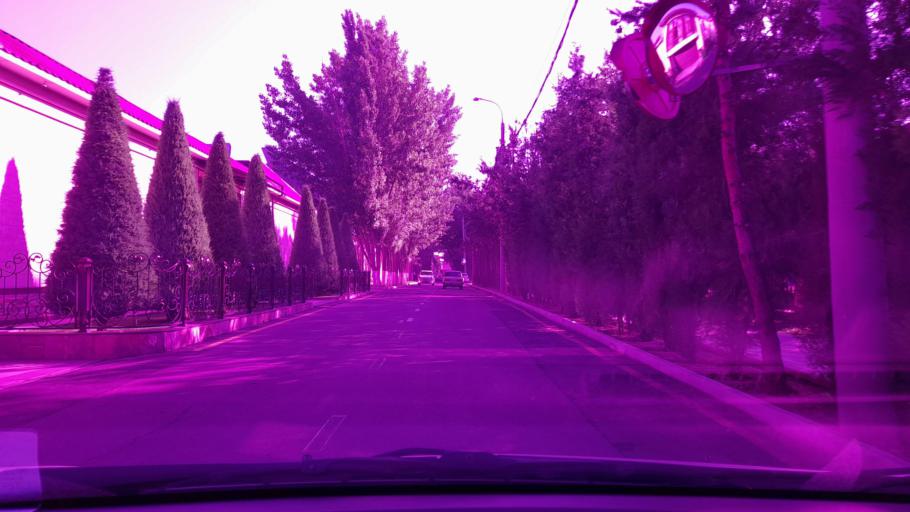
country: UZ
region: Toshkent
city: Salor
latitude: 41.3306
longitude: 69.3604
